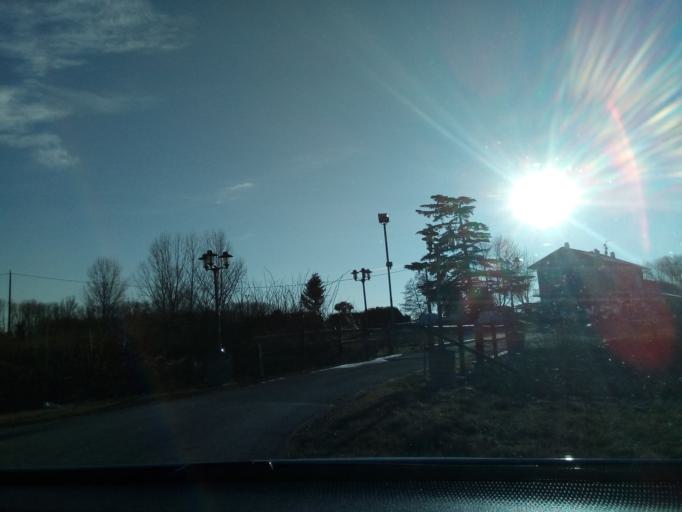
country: IT
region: Piedmont
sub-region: Provincia di Torino
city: Bollengo
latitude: 45.4636
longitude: 7.9310
